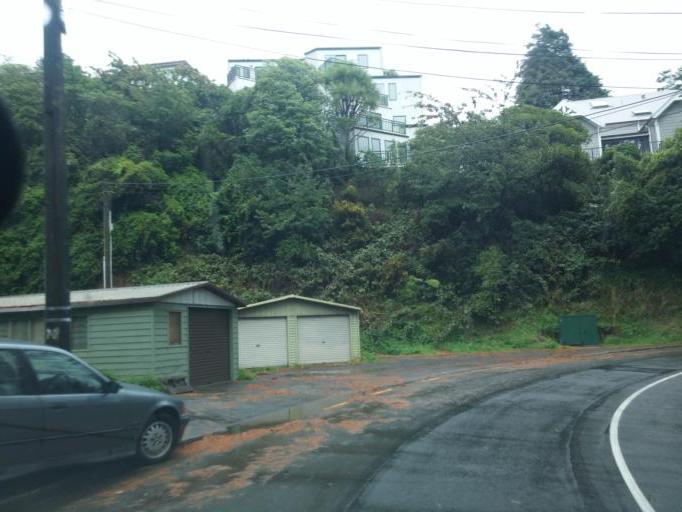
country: NZ
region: Wellington
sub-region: Wellington City
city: Kelburn
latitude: -41.2617
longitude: 174.7705
